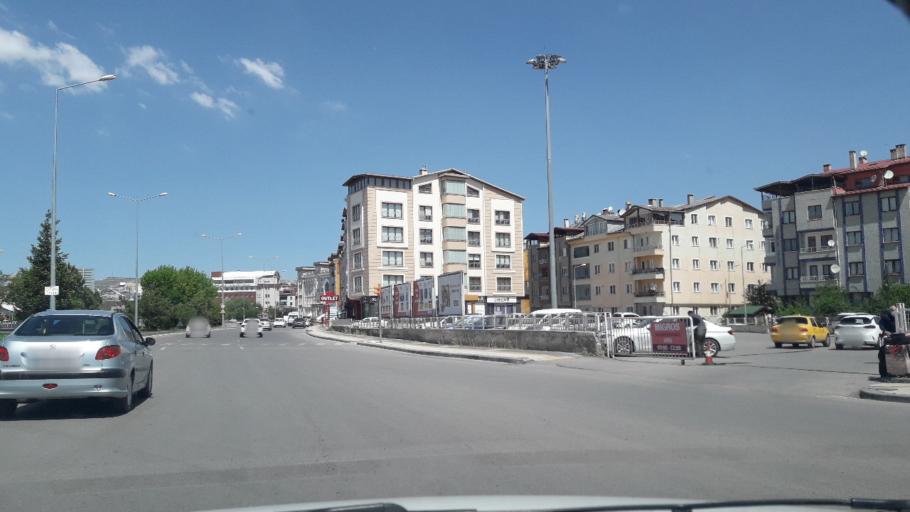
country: TR
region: Sivas
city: Sivas
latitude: 39.7396
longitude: 37.0164
